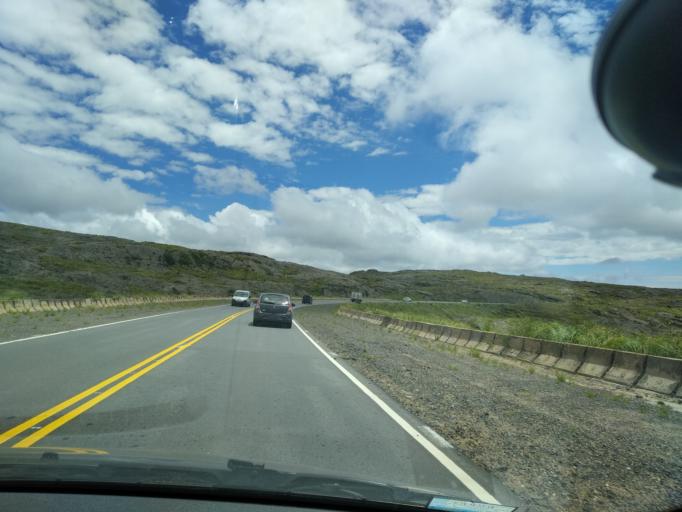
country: AR
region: Cordoba
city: Cuesta Blanca
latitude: -31.6052
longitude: -64.7198
